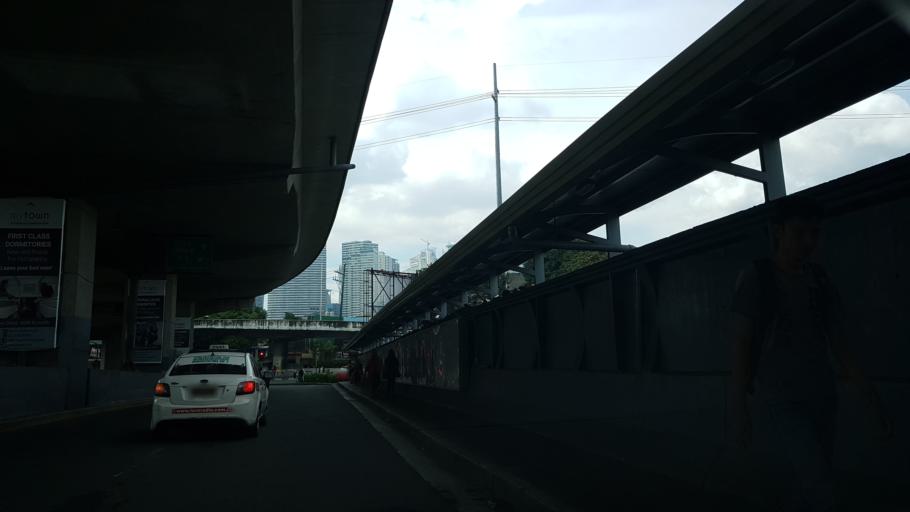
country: PH
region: Metro Manila
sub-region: Makati City
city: Makati City
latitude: 14.5566
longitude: 121.0428
